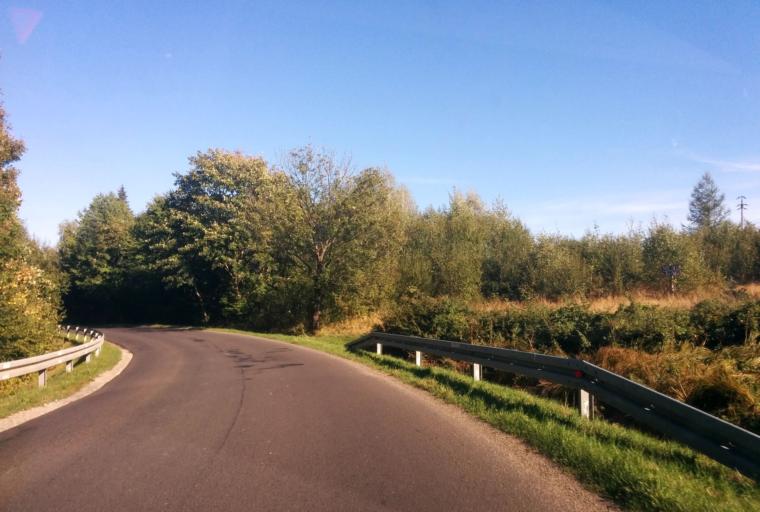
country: PL
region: Subcarpathian Voivodeship
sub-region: Powiat leski
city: Polanczyk
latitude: 49.3370
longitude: 22.4232
